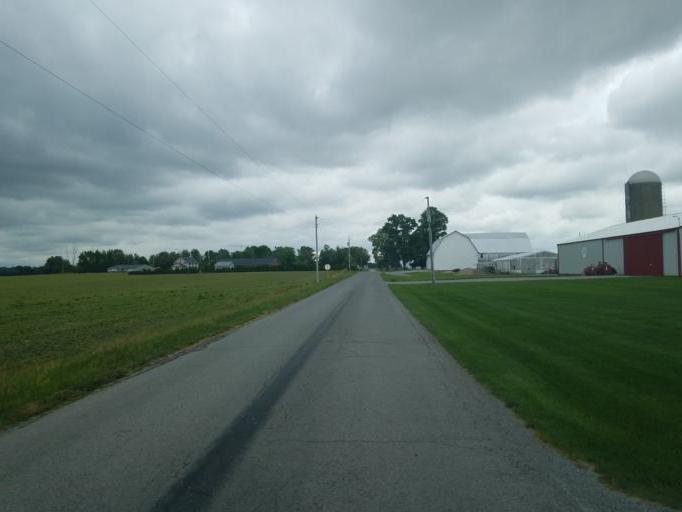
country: US
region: Ohio
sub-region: Crawford County
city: Bucyrus
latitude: 40.7756
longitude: -82.9857
